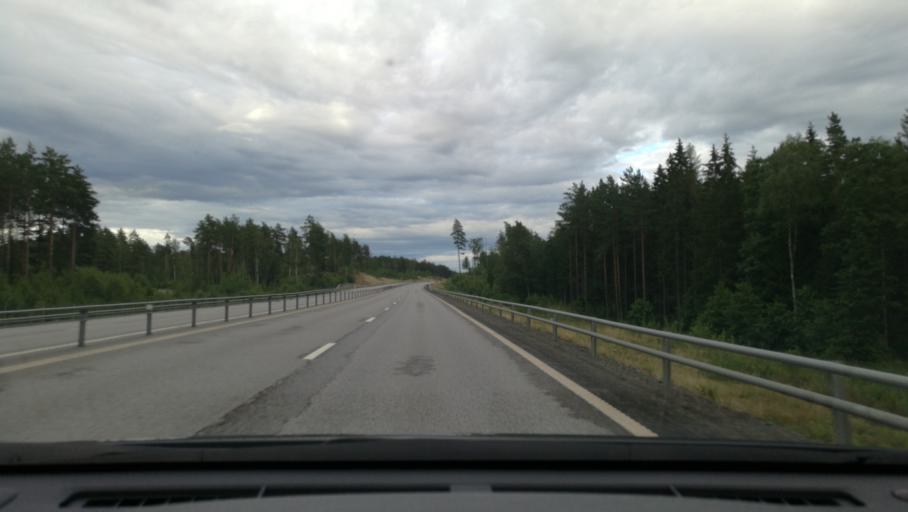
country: SE
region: OEstergoetland
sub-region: Norrkopings Kommun
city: Svartinge
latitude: 58.6678
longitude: 16.0051
